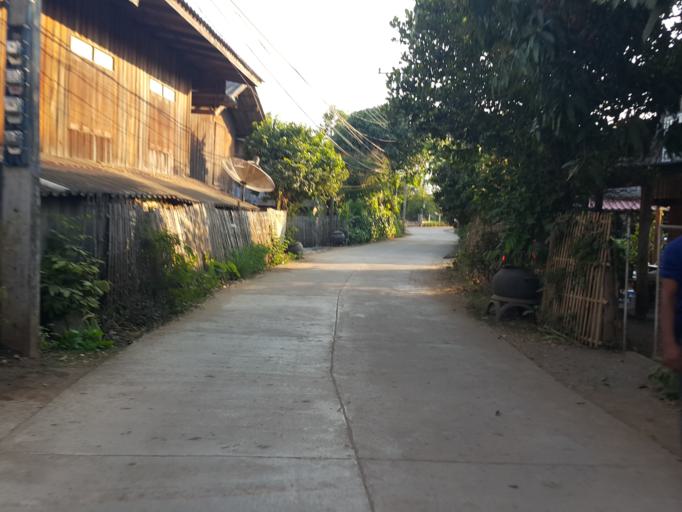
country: TH
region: Chiang Mai
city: Mae On
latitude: 18.7649
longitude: 99.2598
